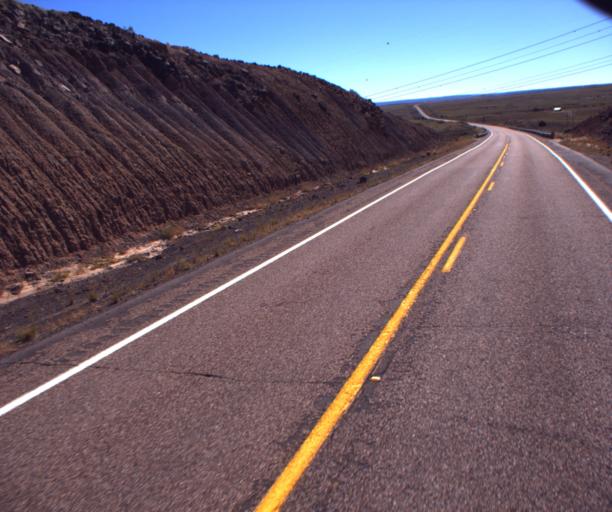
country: US
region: Arizona
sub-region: Apache County
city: Saint Johns
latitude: 34.5536
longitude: -109.4906
